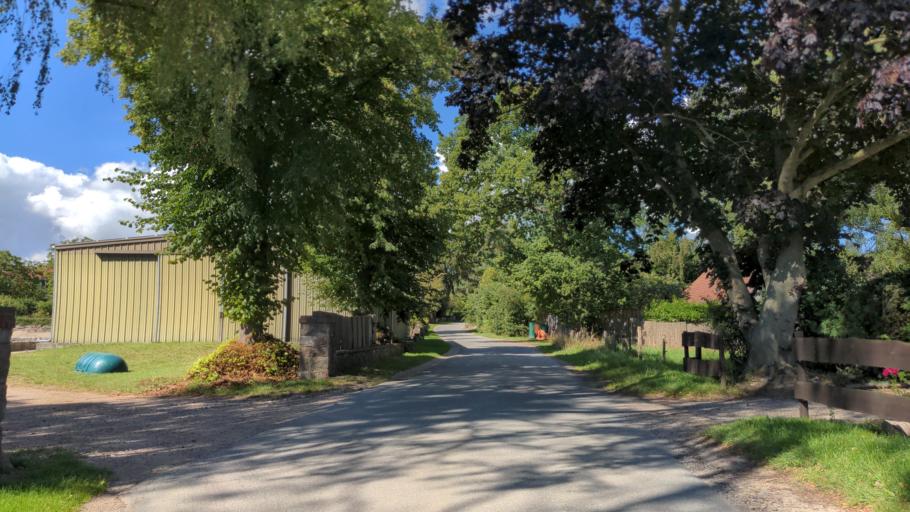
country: DE
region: Schleswig-Holstein
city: Beschendorf
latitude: 54.1774
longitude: 10.8430
